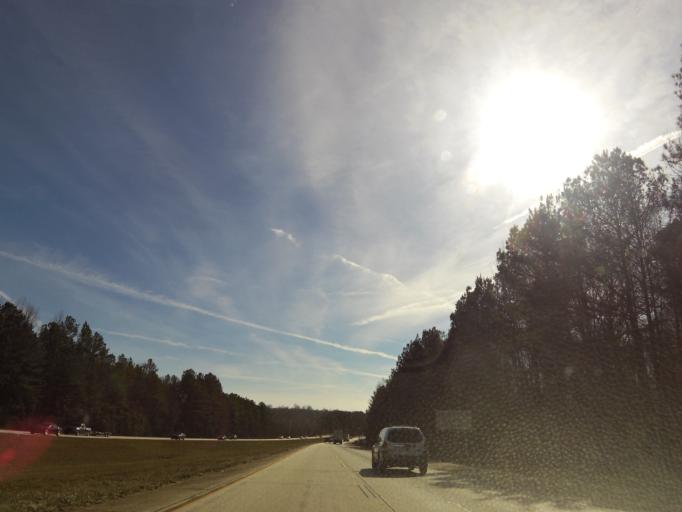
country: US
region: Georgia
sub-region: Troup County
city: Hogansville
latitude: 33.1021
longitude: -84.9071
